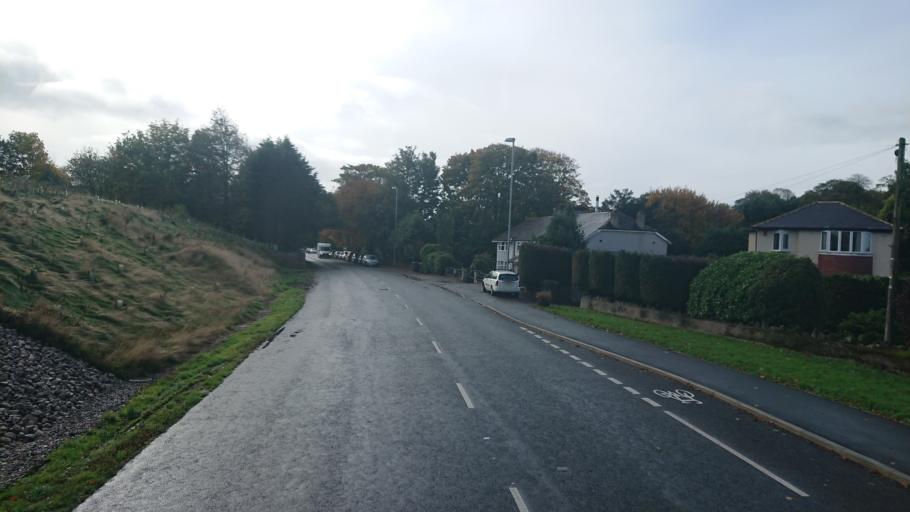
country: GB
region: England
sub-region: Lancashire
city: Bolton le Sands
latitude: 54.0696
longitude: -2.8013
